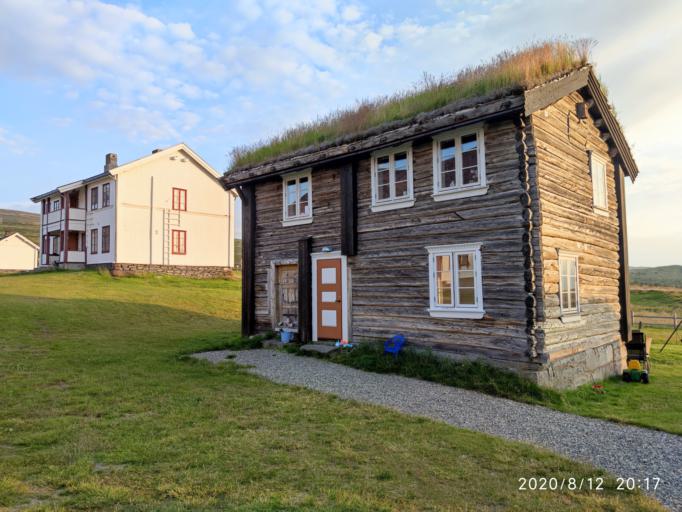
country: NO
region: Oppland
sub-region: Dovre
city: Dovre
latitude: 62.1140
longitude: 9.2865
